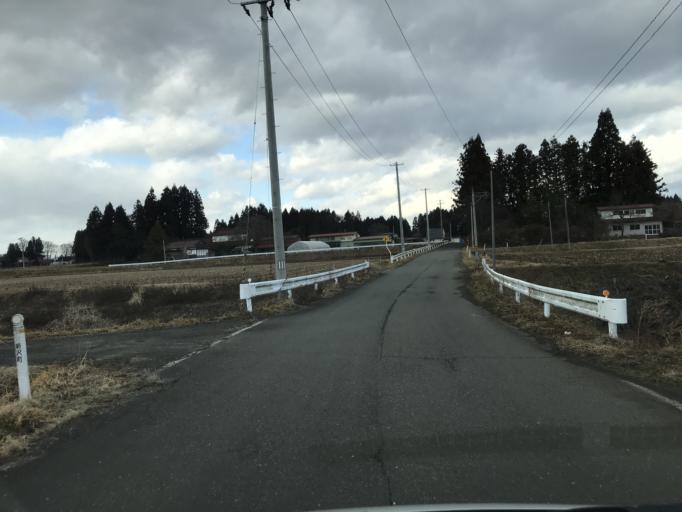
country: JP
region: Iwate
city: Mizusawa
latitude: 39.0807
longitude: 141.1112
